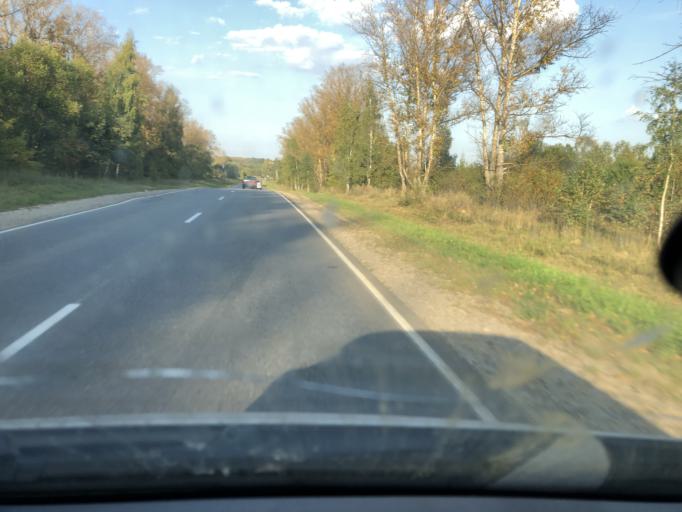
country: RU
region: Kaluga
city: Peremyshl'
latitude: 54.2236
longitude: 36.0359
